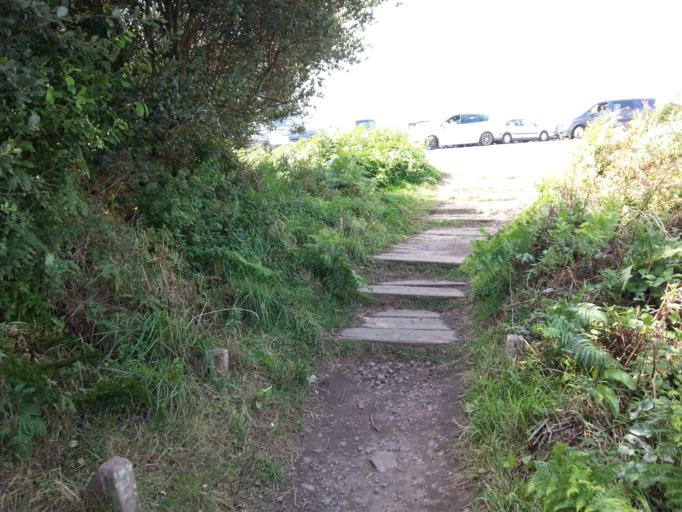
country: FR
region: Brittany
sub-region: Departement des Cotes-d'Armor
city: Saint-Cast-le-Guildo
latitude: 48.6832
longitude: -2.3184
